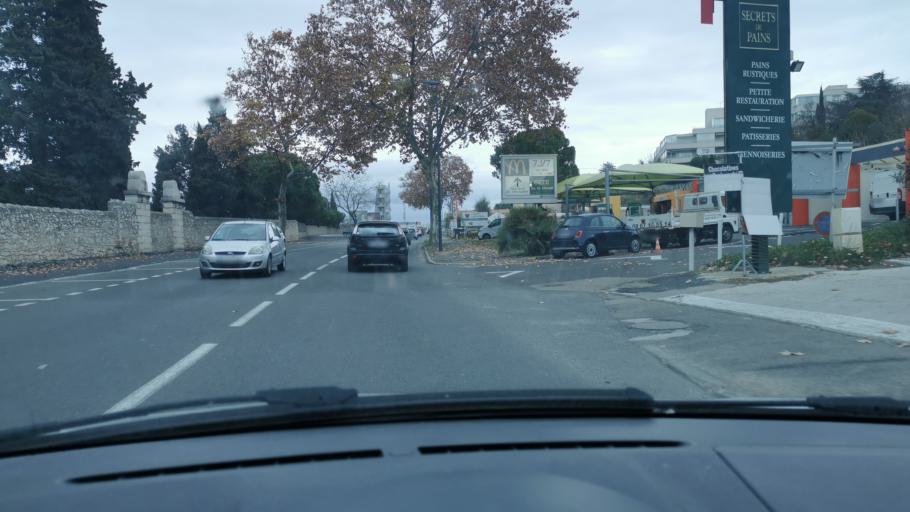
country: FR
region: Languedoc-Roussillon
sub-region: Departement de l'Herault
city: Sete
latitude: 43.4047
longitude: 3.6629
